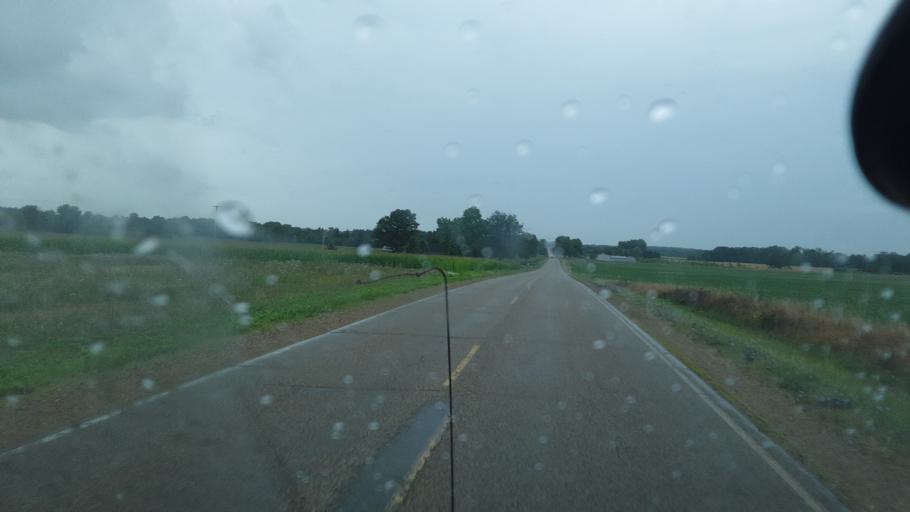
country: US
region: Michigan
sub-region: Hillsdale County
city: Reading
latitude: 41.7081
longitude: -84.7367
